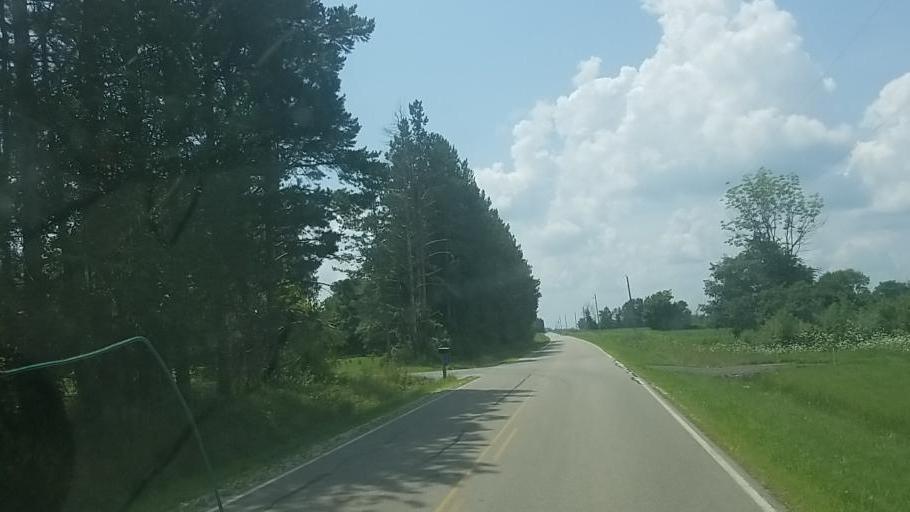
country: US
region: Ohio
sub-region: Crawford County
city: Bucyrus
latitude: 40.7549
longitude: -83.0660
